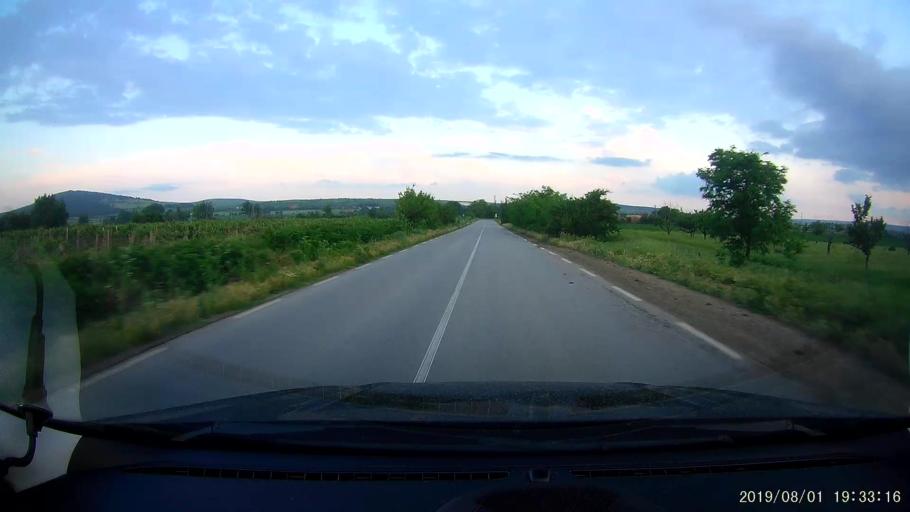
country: BG
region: Burgas
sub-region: Obshtina Sungurlare
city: Sungurlare
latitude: 42.7827
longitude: 26.8755
